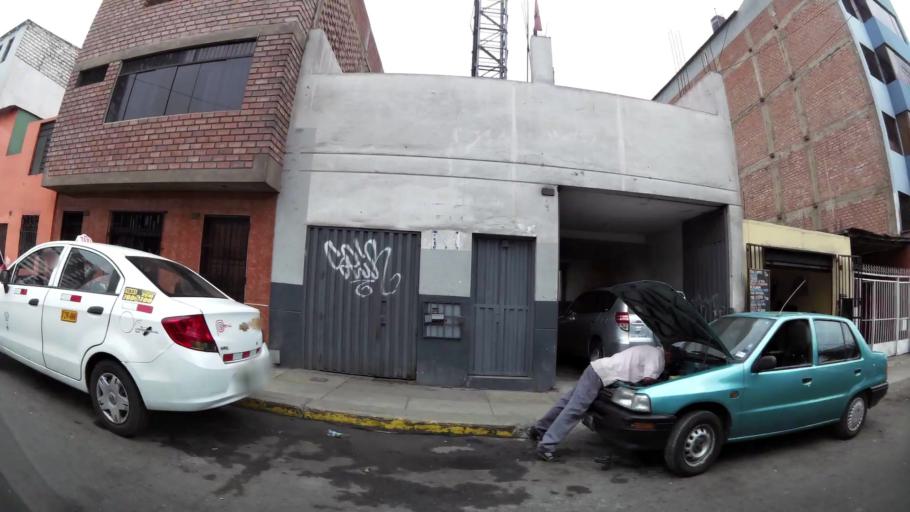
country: PE
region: Lima
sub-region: Lima
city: San Isidro
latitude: -12.0843
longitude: -77.0403
